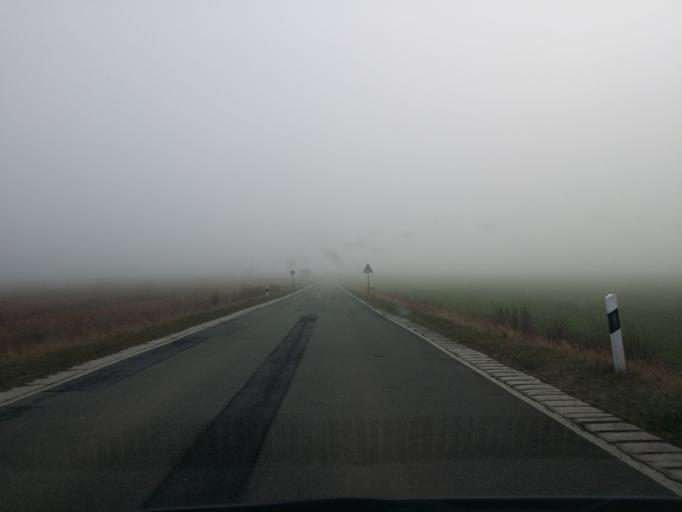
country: DE
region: Schleswig-Holstein
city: Fehmarn
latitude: 54.4245
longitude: 11.1341
